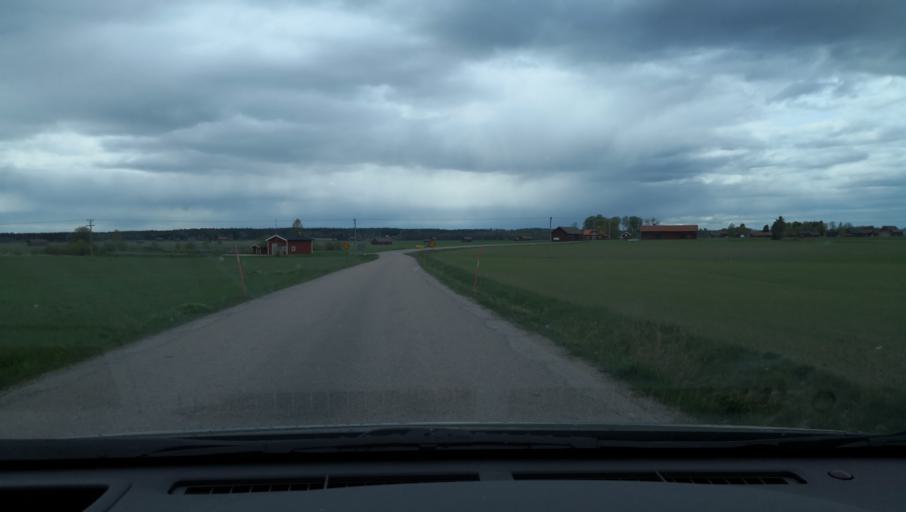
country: SE
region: Dalarna
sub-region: Avesta Kommun
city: Avesta
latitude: 60.0233
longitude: 16.3258
